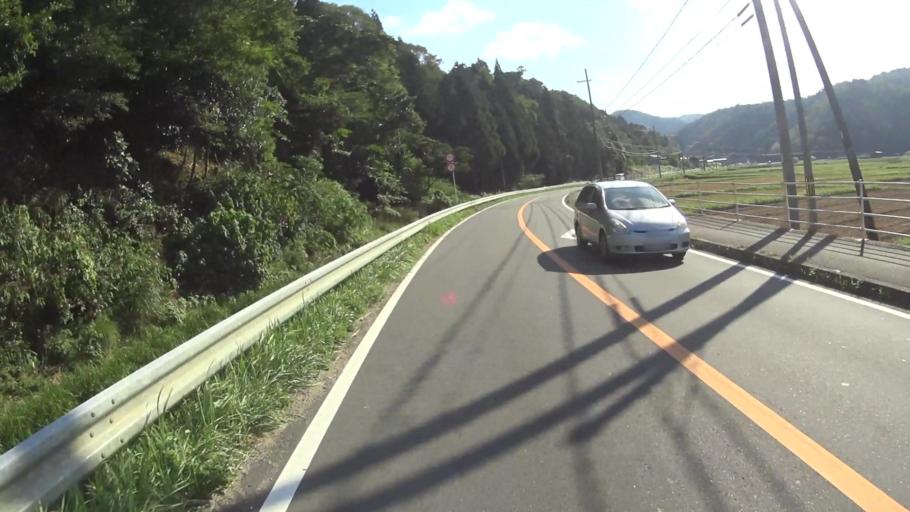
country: JP
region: Kyoto
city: Miyazu
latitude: 35.6629
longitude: 135.0235
